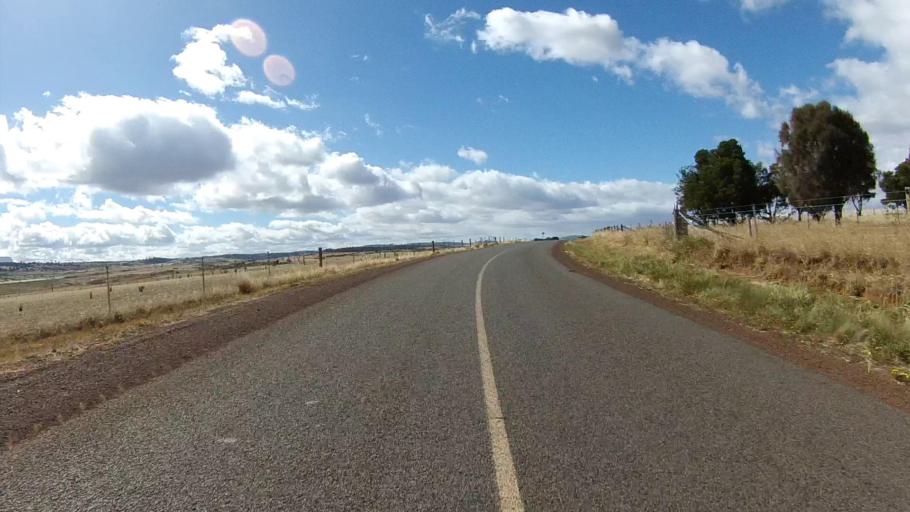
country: AU
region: Tasmania
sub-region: Northern Midlands
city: Evandale
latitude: -41.7077
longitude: 147.4045
